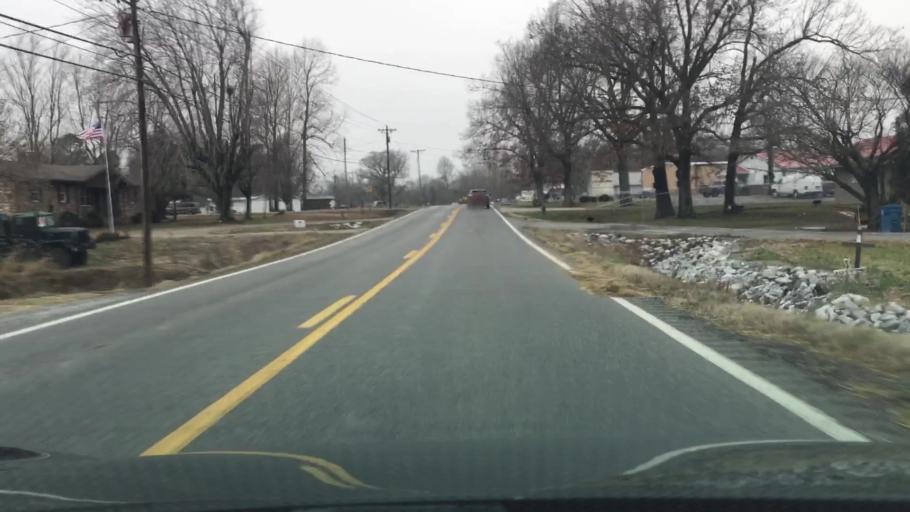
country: US
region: Kentucky
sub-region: Marshall County
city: Calvert City
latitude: 36.9730
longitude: -88.3978
